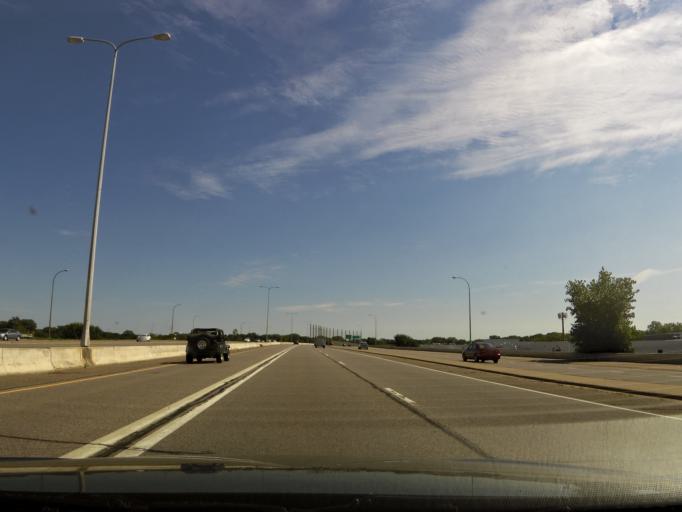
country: US
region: Minnesota
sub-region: Hennepin County
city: Saint Louis Park
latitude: 44.9738
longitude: -93.3962
